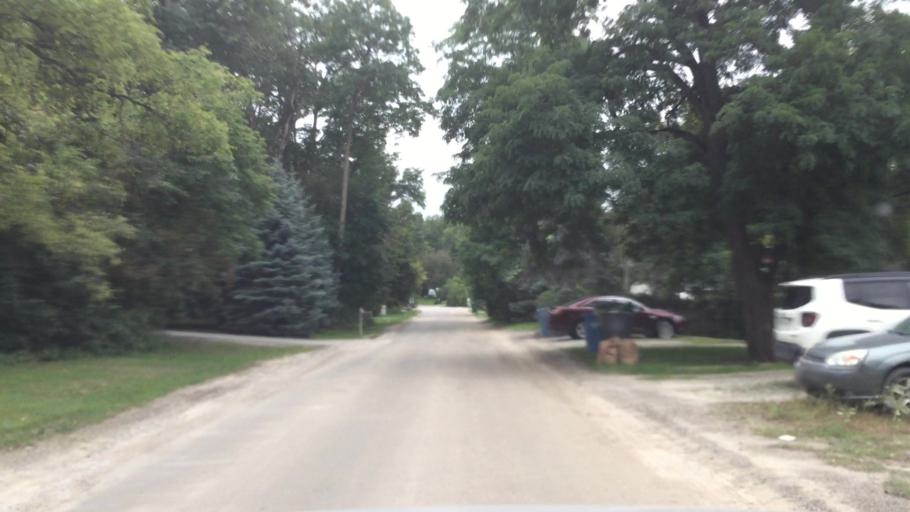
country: US
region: Michigan
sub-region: Livingston County
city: Whitmore Lake
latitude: 42.4663
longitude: -83.7981
